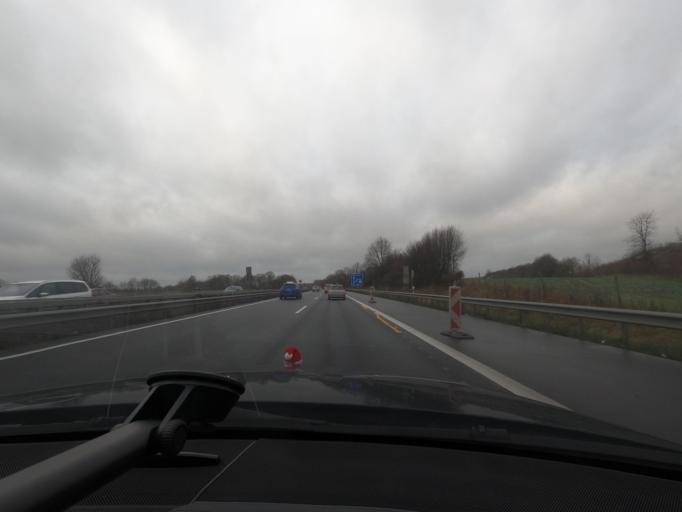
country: DE
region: Schleswig-Holstein
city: Schonbek
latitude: 54.1745
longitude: 9.9562
